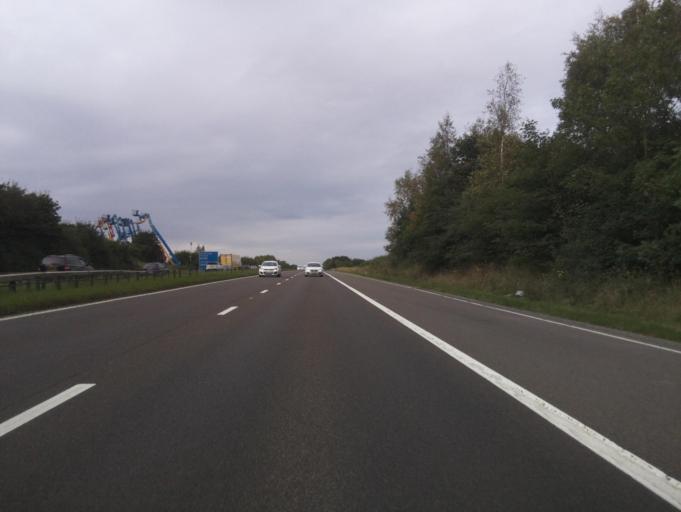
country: GB
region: England
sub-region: County Durham
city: Durham
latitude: 54.7757
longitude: -1.5327
